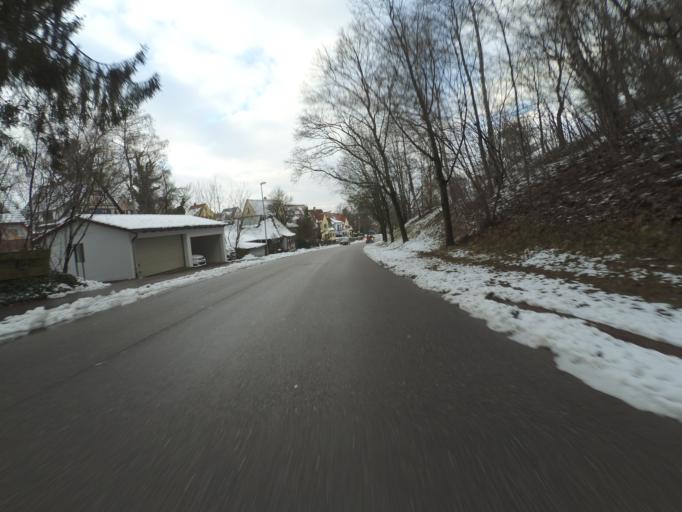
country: DE
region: Baden-Wuerttemberg
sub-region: Regierungsbezirk Stuttgart
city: Aalen
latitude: 48.8278
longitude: 10.0971
